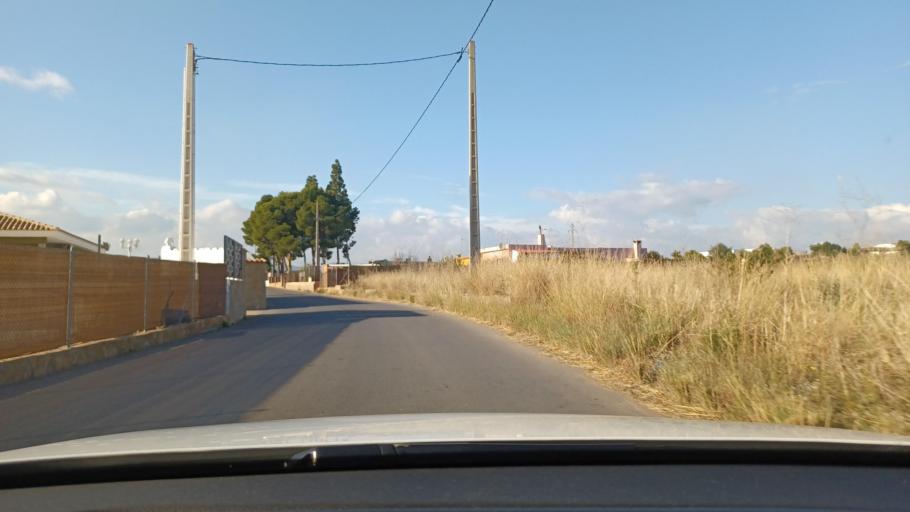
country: ES
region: Valencia
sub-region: Provincia de Castello
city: Onda
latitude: 39.9506
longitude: -0.2272
